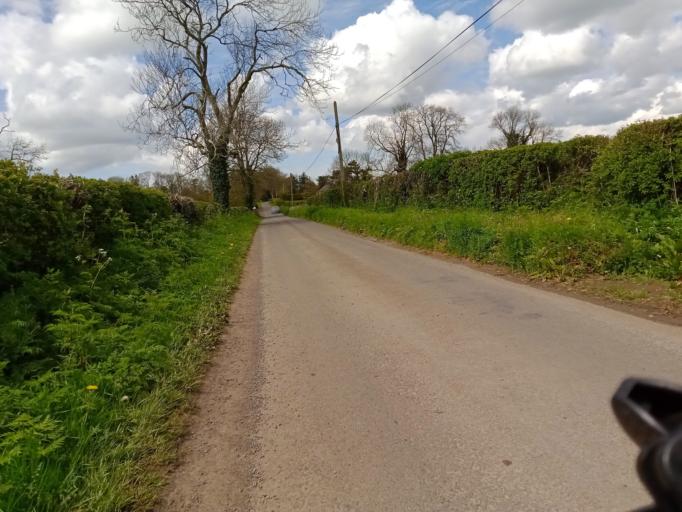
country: IE
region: Leinster
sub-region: Kilkenny
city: Thomastown
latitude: 52.5834
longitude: -7.1357
